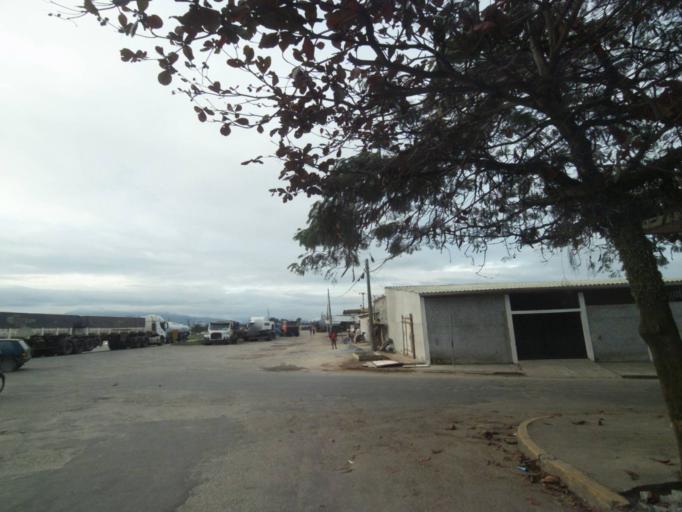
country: BR
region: Parana
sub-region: Paranagua
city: Paranagua
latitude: -25.5302
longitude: -48.5484
